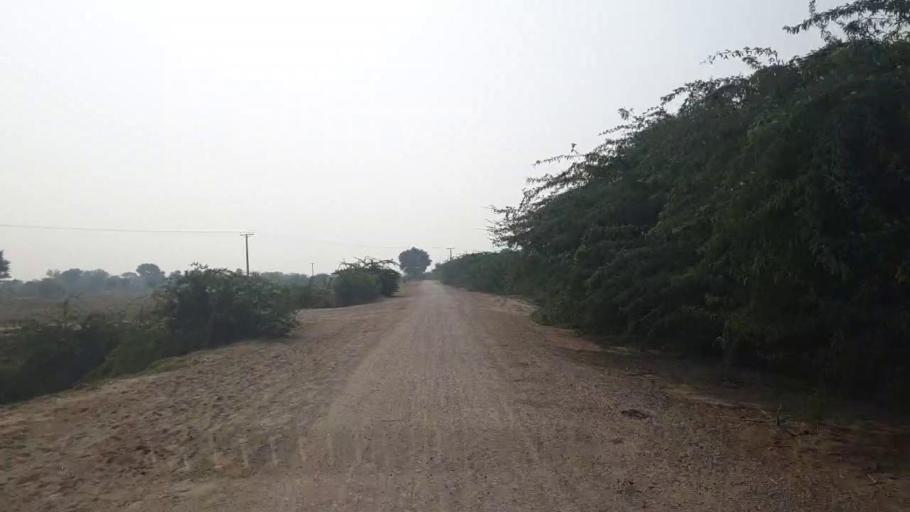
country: PK
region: Sindh
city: Tando Muhammad Khan
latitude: 25.2636
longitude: 68.5115
